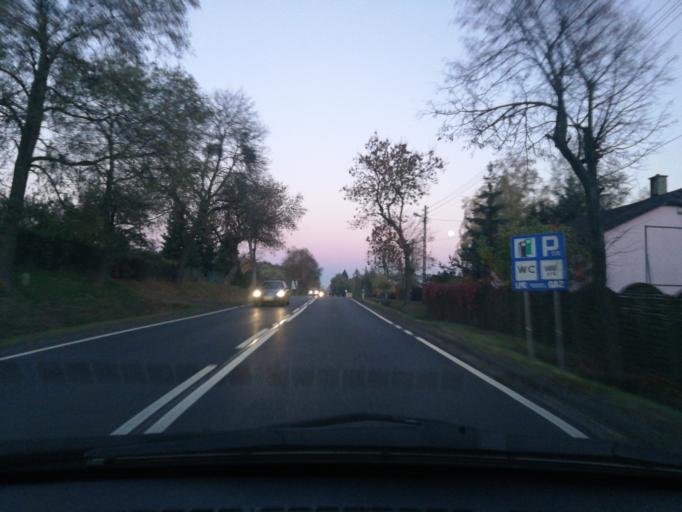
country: PL
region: Lodz Voivodeship
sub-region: Powiat brzezinski
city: Brzeziny
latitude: 51.8046
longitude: 19.6903
